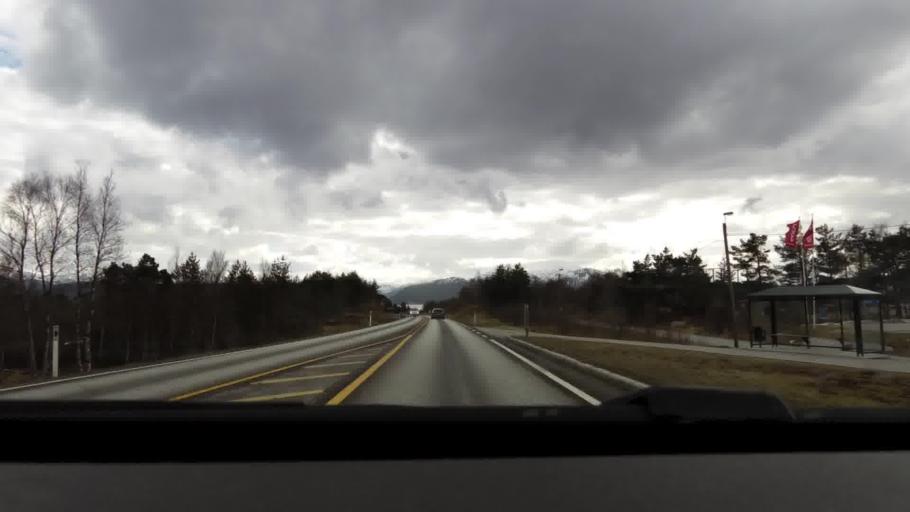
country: NO
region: More og Romsdal
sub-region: Kristiansund
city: Rensvik
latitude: 63.0380
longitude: 7.7872
